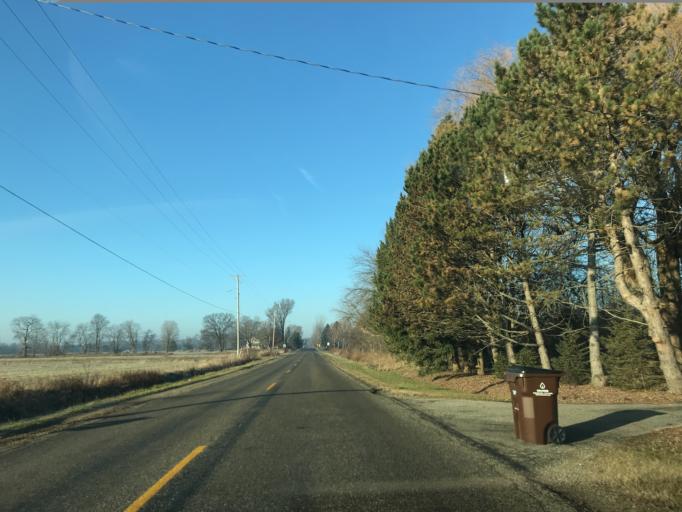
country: US
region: Michigan
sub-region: Eaton County
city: Dimondale
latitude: 42.6620
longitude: -84.6291
